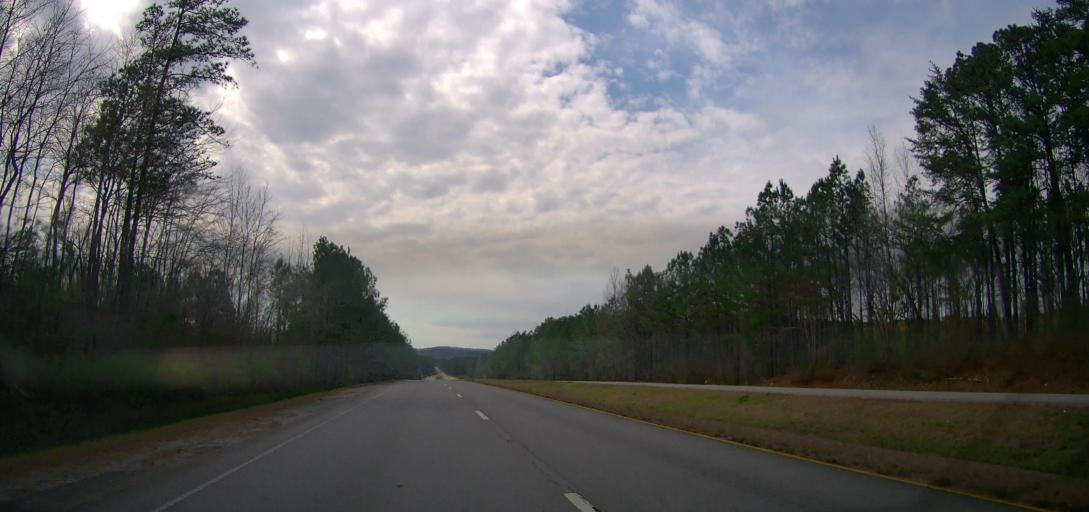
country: US
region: Alabama
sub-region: Marion County
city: Winfield
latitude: 33.9320
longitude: -87.6997
